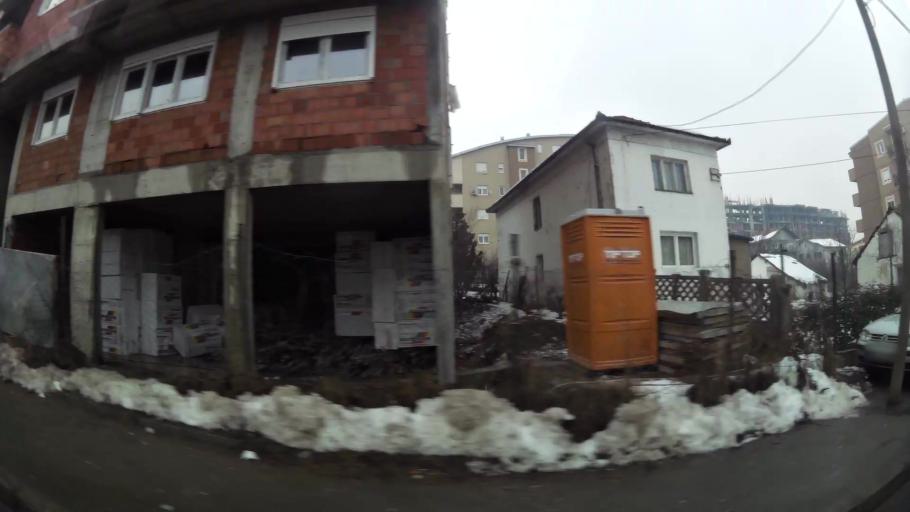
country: RS
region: Central Serbia
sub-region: Belgrade
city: Zvezdara
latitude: 44.7675
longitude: 20.5137
